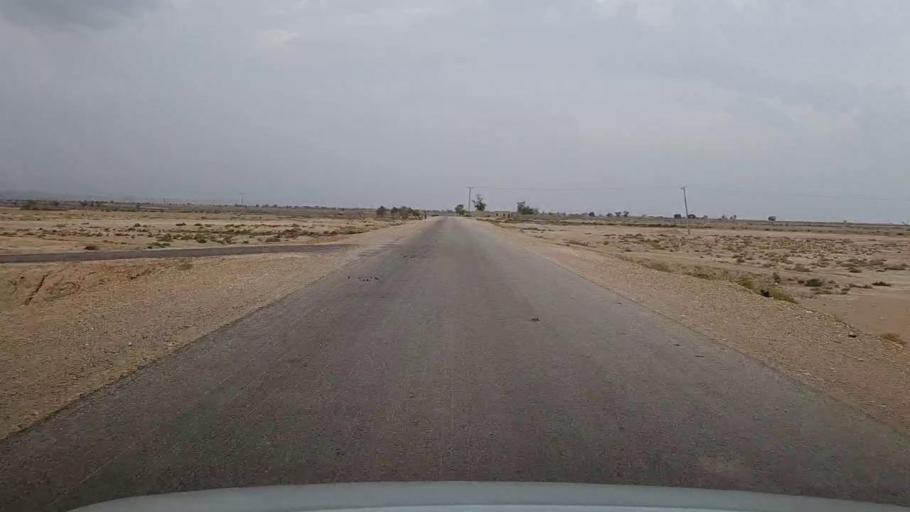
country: PK
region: Sindh
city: Sehwan
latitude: 26.3367
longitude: 67.7156
